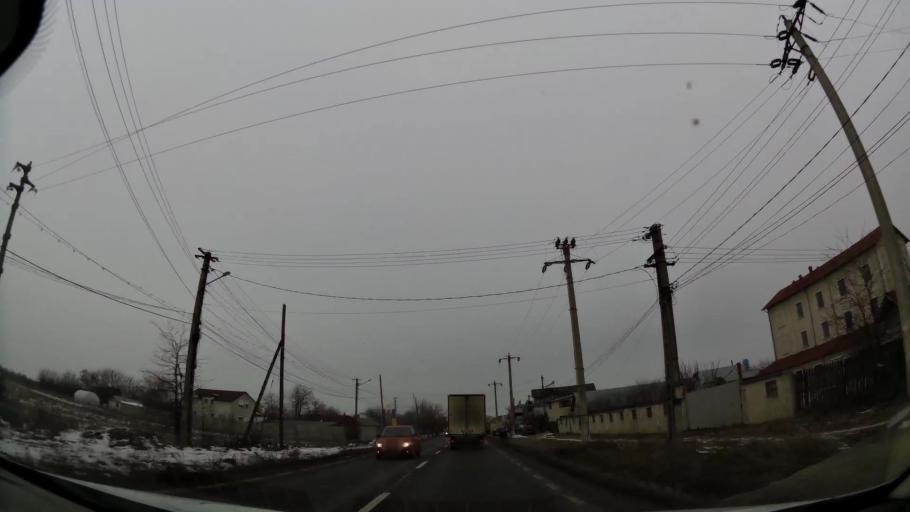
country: RO
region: Dambovita
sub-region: Comuna Racari
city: Racari
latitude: 44.6202
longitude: 25.7545
